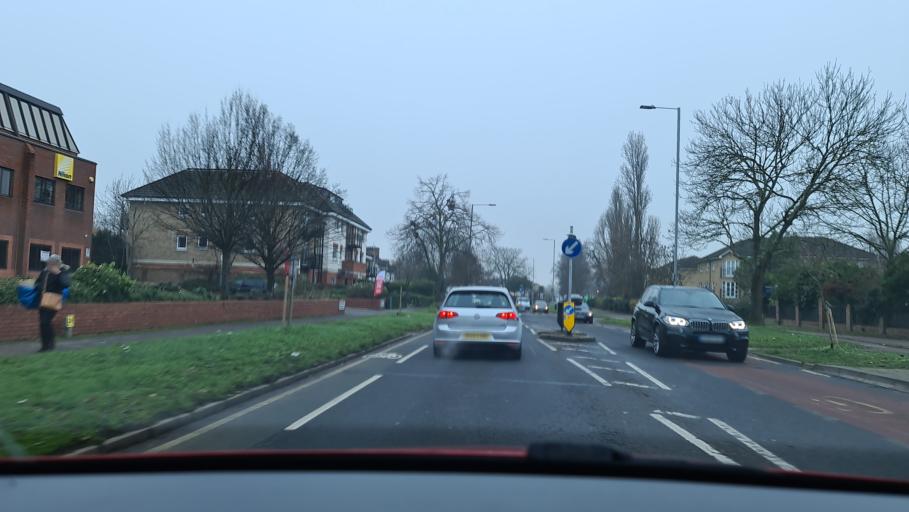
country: GB
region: England
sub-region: Greater London
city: Kingston upon Thames
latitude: 51.4291
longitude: -0.3069
